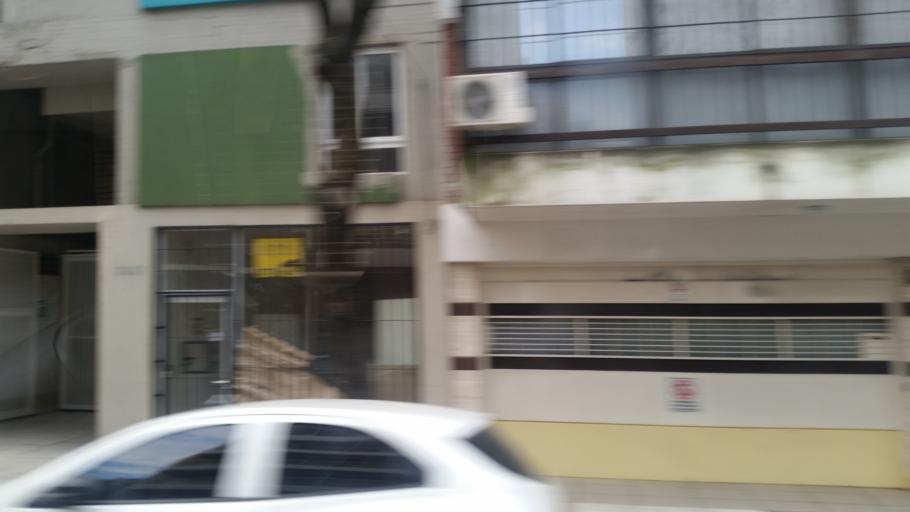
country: AR
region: Buenos Aires F.D.
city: Buenos Aires
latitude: -34.6071
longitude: -58.4207
